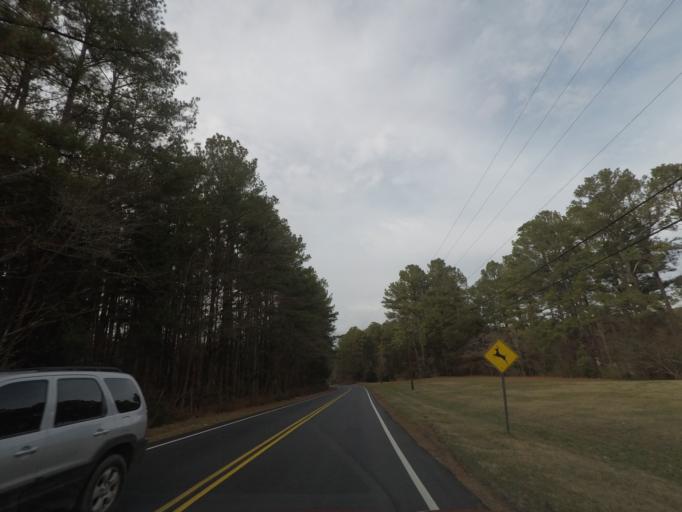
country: US
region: North Carolina
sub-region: Durham County
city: Durham
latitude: 36.0554
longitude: -78.9749
